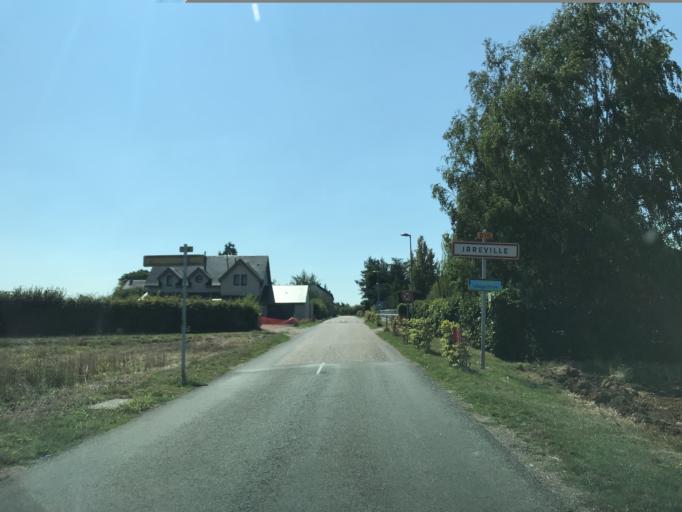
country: FR
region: Haute-Normandie
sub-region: Departement de l'Eure
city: Heudreville-sur-Eure
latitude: 49.0977
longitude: 1.2091
